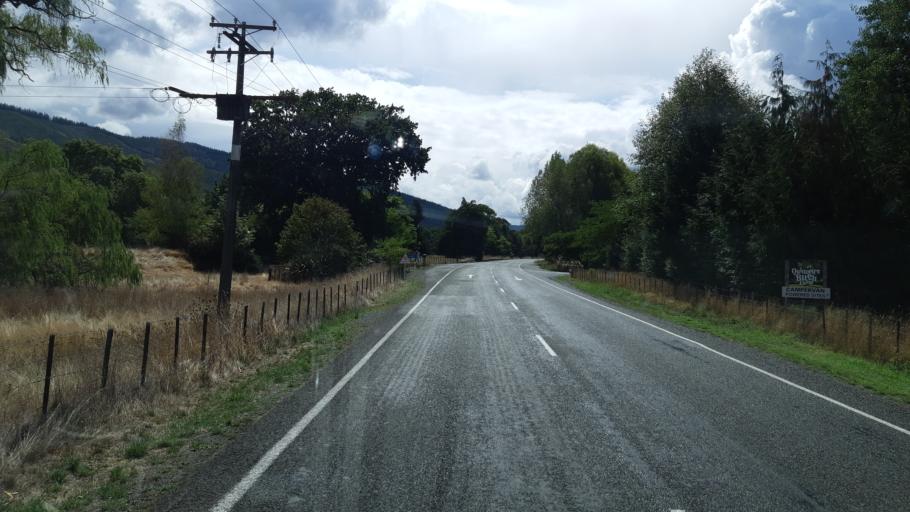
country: NZ
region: Tasman
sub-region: Tasman District
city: Wakefield
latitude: -41.4599
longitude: 172.8113
